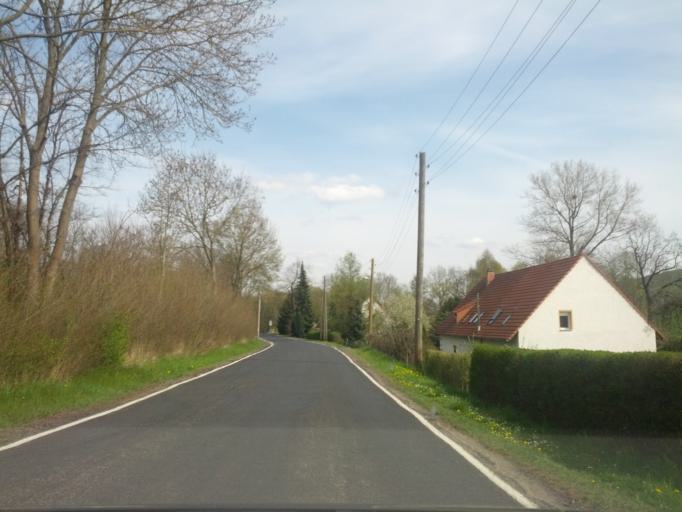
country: DE
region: Thuringia
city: Seebach
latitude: 50.9799
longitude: 10.4368
